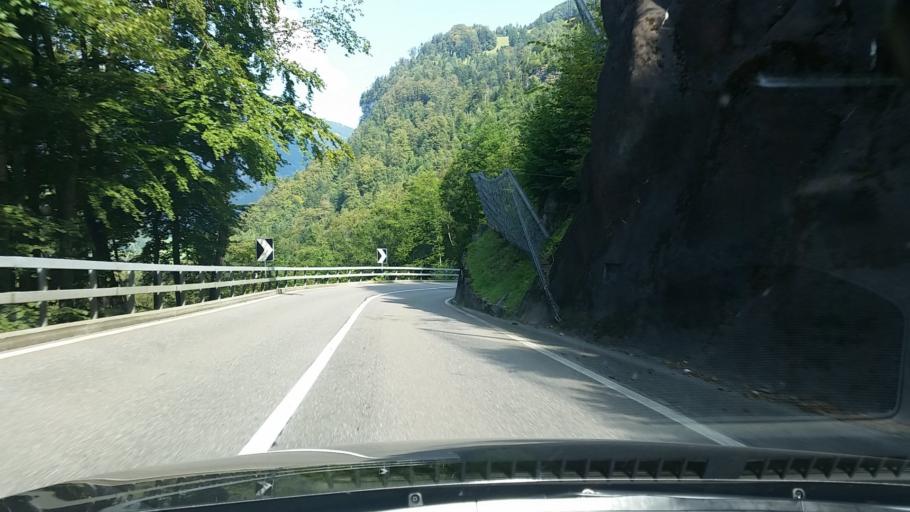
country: CH
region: Obwalden
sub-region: Obwalden
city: Engelberg
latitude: 46.8416
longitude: 8.3761
